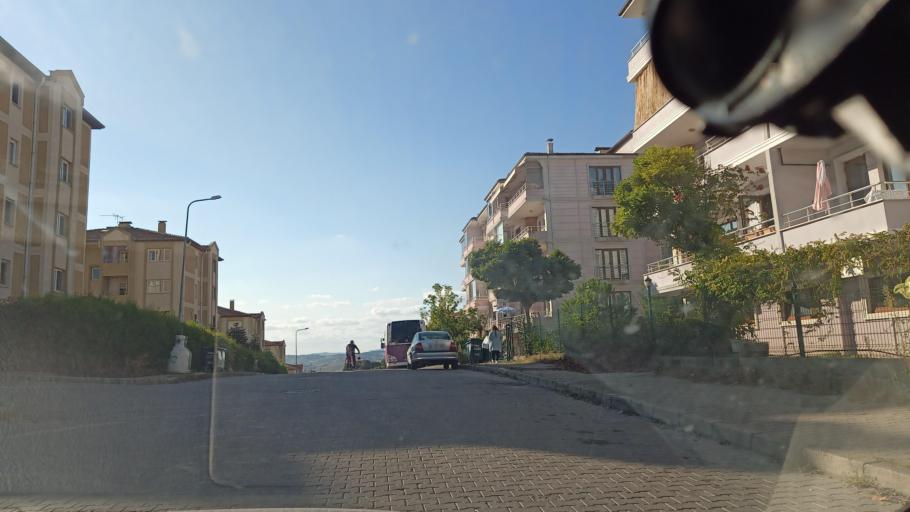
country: TR
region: Kocaeli
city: Kaymaz
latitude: 40.8604
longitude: 30.2917
